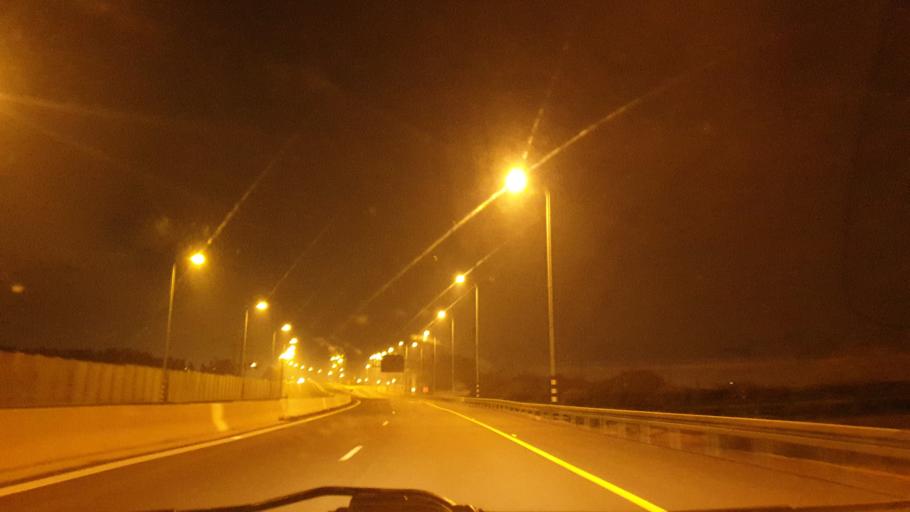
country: IL
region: Central District
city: Ramla
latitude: 31.9470
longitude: 34.8590
